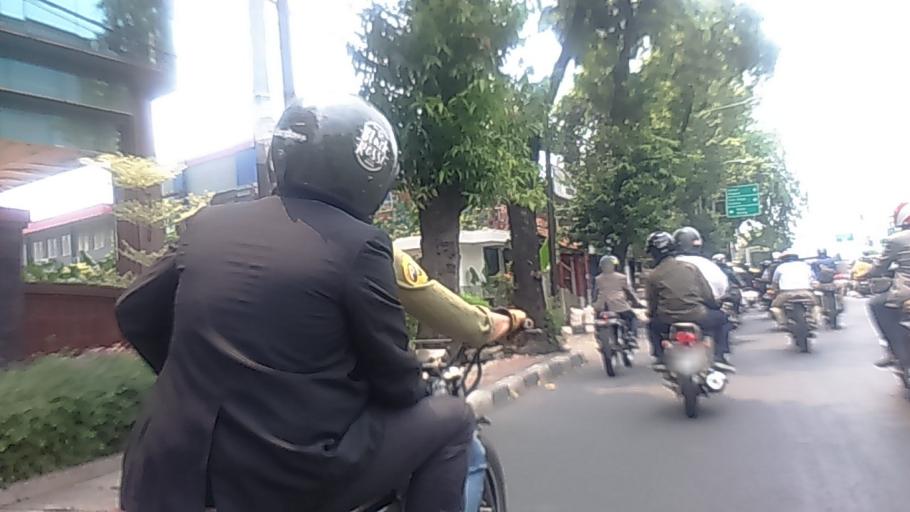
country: ID
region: Jakarta Raya
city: Jakarta
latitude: -6.2616
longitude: 106.8293
